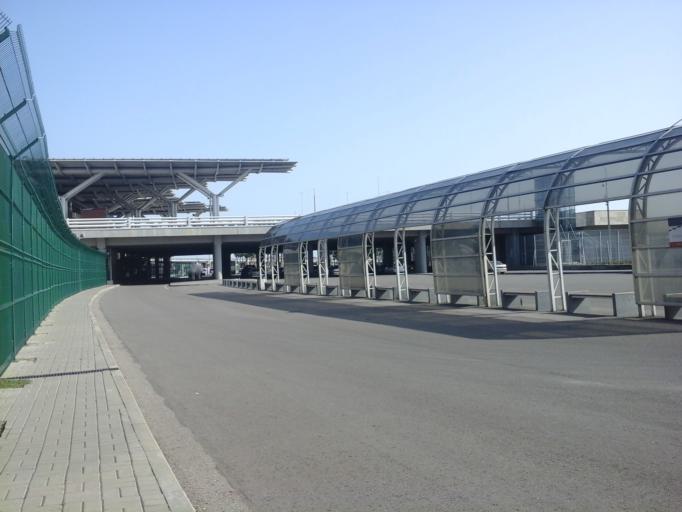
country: RU
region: Krasnodarskiy
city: Adler
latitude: 43.4120
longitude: 39.9722
